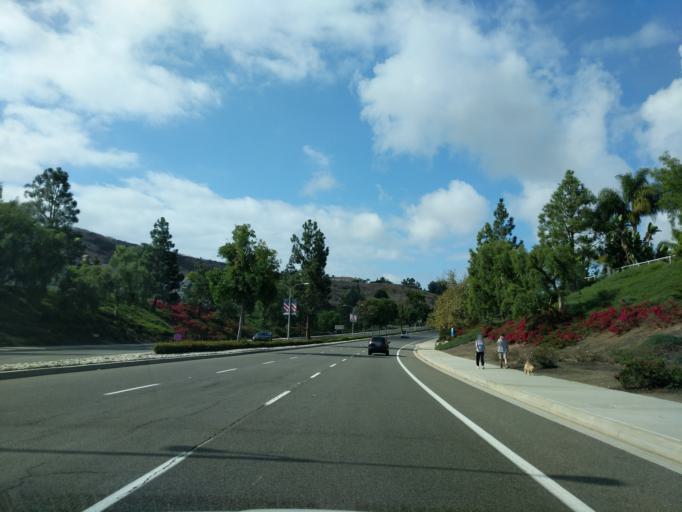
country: US
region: California
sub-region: Orange County
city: San Juan Capistrano
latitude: 33.5076
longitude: -117.6847
